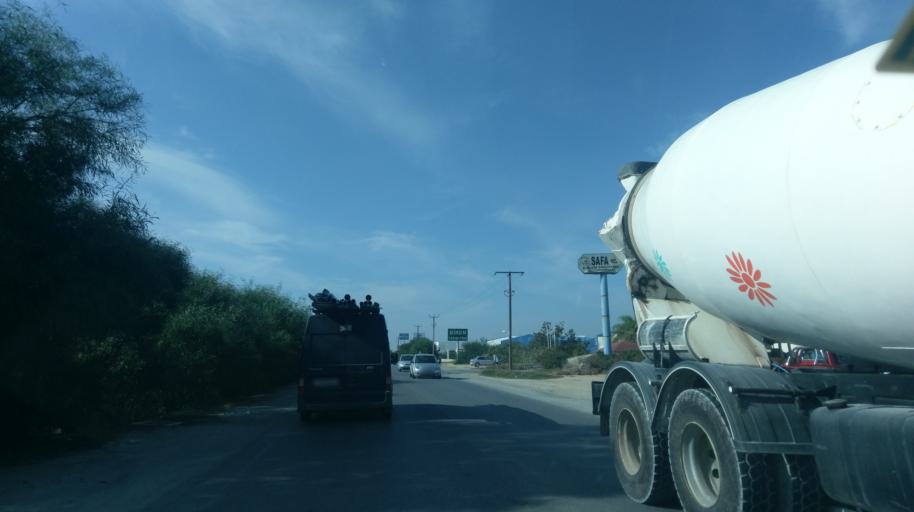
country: CY
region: Ammochostos
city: Famagusta
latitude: 35.1451
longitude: 33.8928
